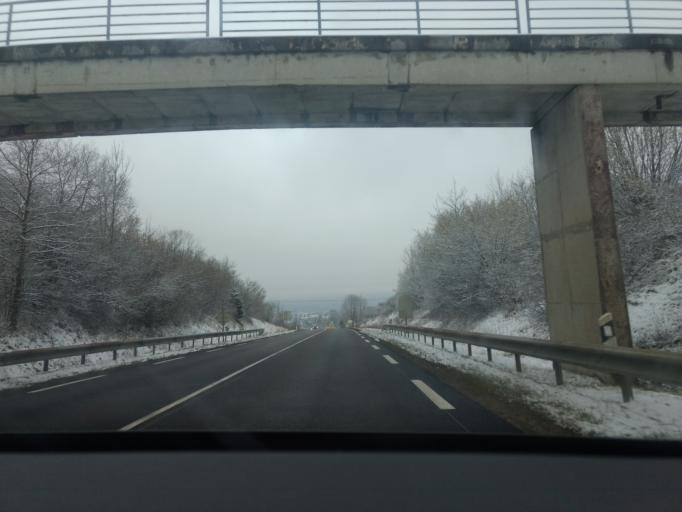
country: FR
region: Franche-Comte
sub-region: Departement du Jura
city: Champagnole
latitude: 46.7697
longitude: 5.9049
